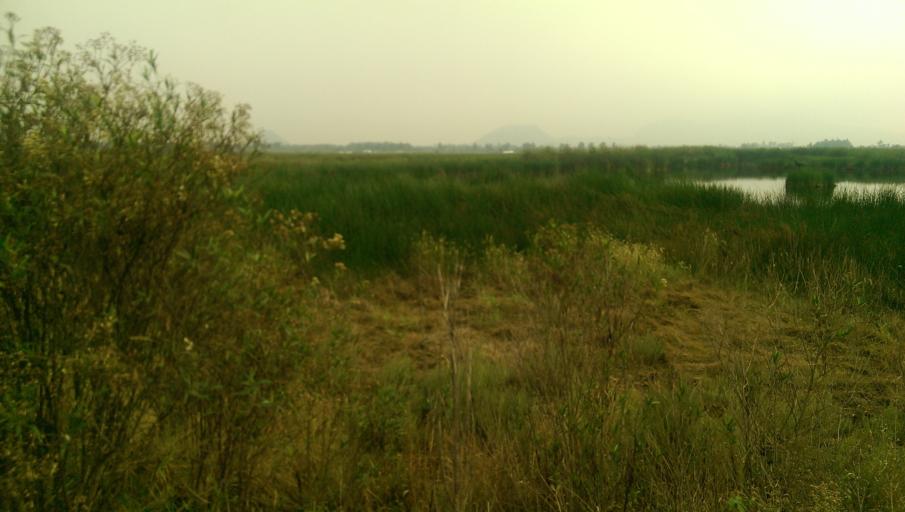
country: MX
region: Mexico City
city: Tlahuac
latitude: 19.2645
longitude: -99.0495
